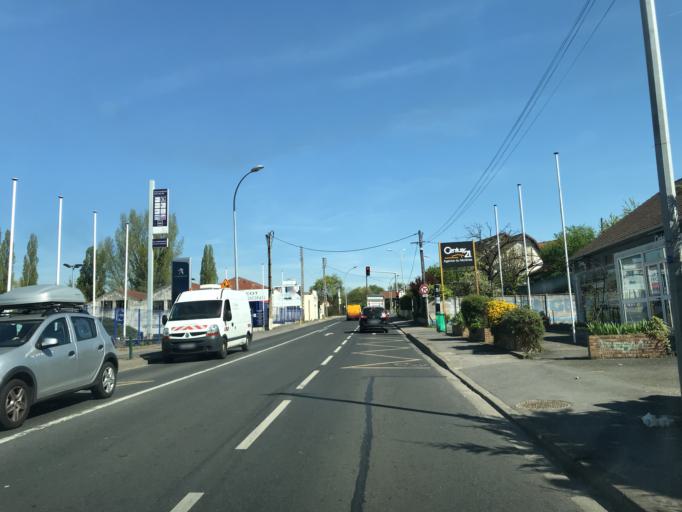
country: FR
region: Ile-de-France
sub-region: Departement du Val-de-Marne
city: Saint-Maur-des-Fosses
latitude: 48.7799
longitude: 2.5121
